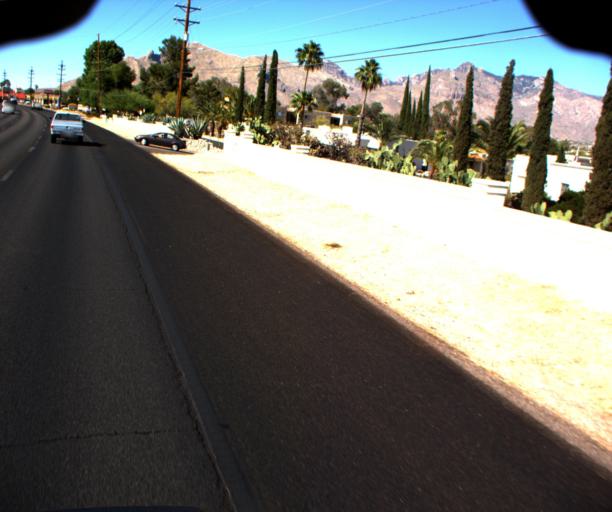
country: US
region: Arizona
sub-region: Pima County
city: Casas Adobes
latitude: 32.3177
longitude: -110.9754
